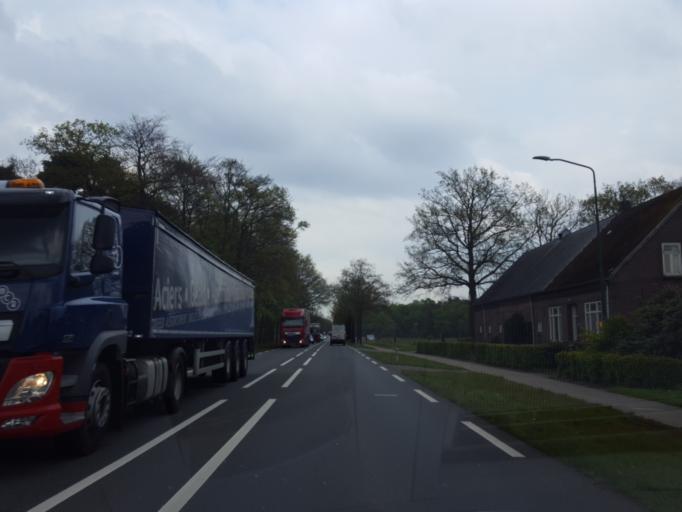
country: NL
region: North Brabant
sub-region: Gemeente Valkenswaard
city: Valkenswaard
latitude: 51.3520
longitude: 5.5061
